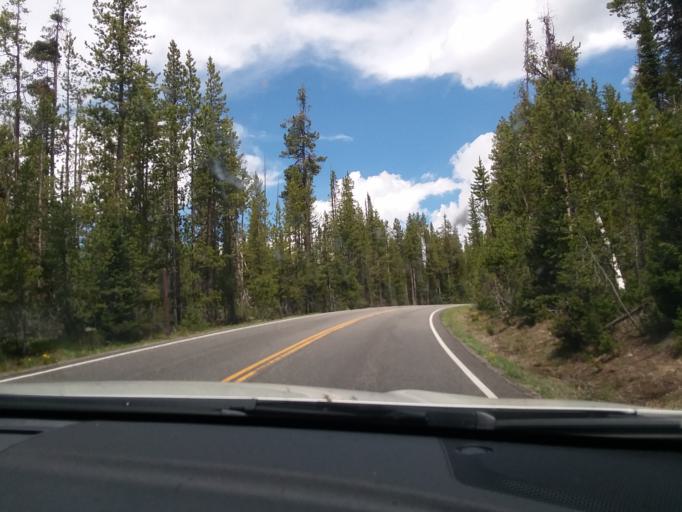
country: US
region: Idaho
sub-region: Teton County
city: Driggs
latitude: 44.1533
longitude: -110.6746
